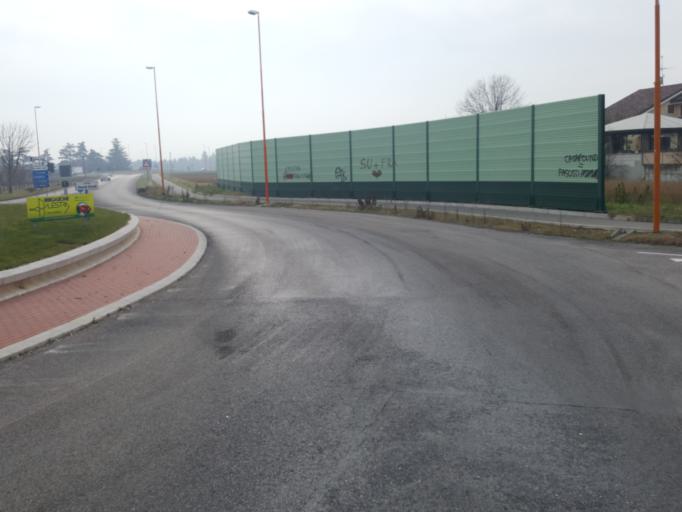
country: IT
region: Emilia-Romagna
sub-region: Forli-Cesena
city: Cesena
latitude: 44.1525
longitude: 12.2694
